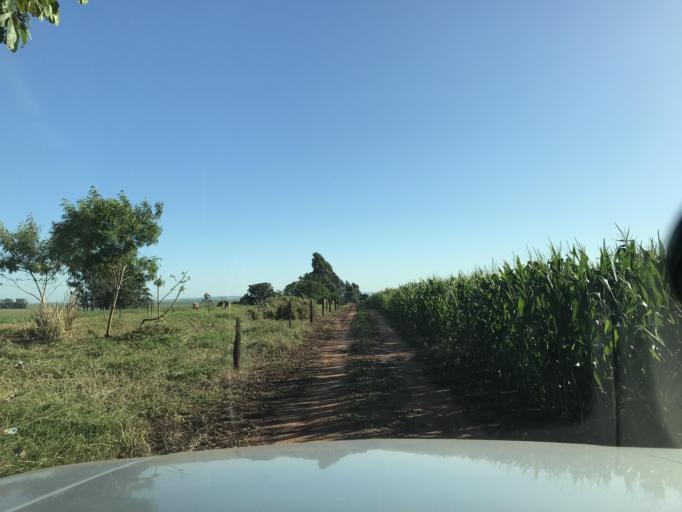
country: BR
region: Parana
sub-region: Palotina
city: Palotina
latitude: -24.2141
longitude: -53.7585
